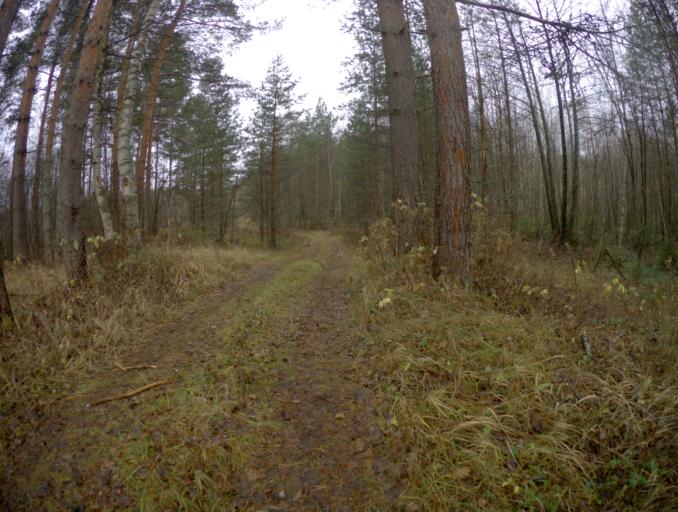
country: RU
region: Vladimir
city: Golovino
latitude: 56.0147
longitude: 40.4834
